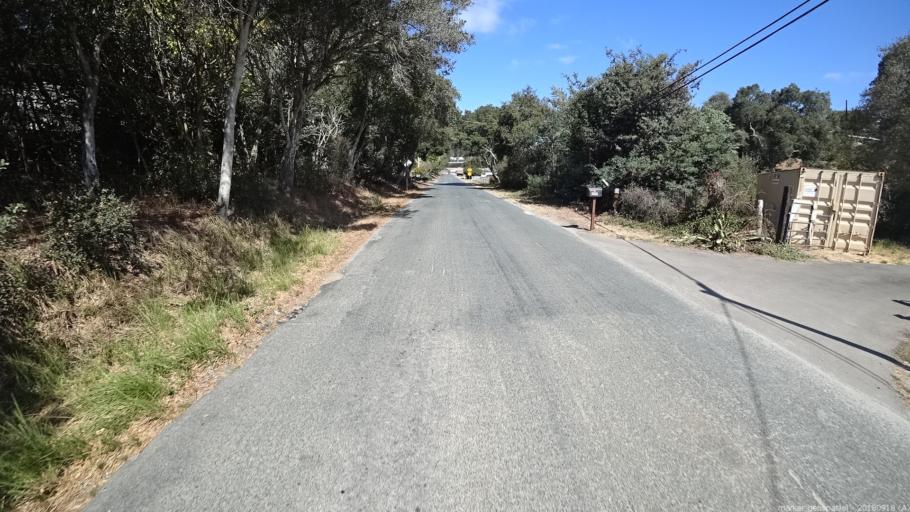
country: US
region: California
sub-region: Monterey County
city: Prunedale
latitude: 36.7854
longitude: -121.6705
